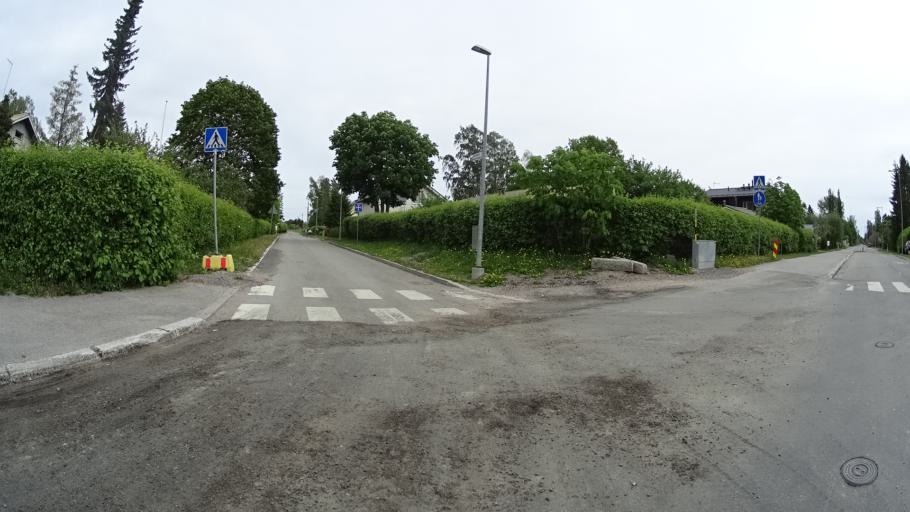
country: FI
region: Uusimaa
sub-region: Helsinki
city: Vantaa
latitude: 60.2985
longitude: 25.0037
